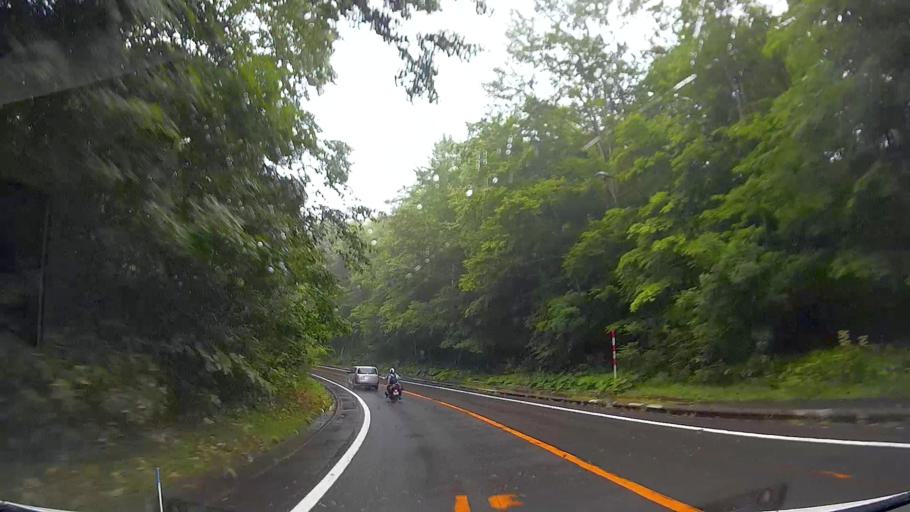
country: JP
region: Hokkaido
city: Shiraoi
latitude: 42.7690
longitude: 141.4142
